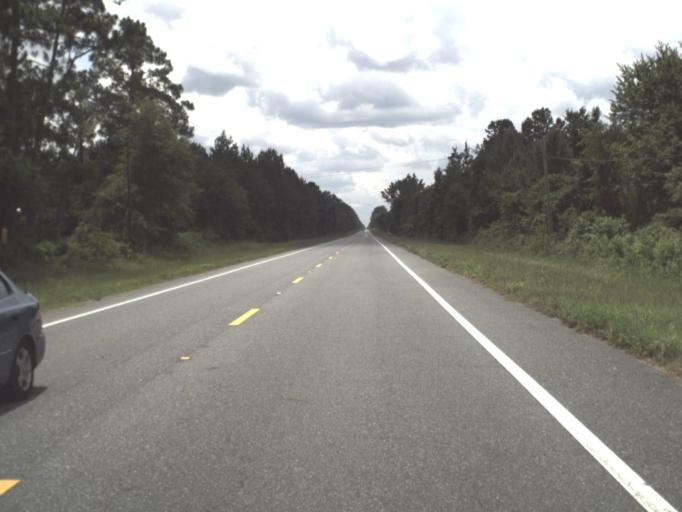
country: US
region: Florida
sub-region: Columbia County
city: Watertown
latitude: 30.1577
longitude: -82.5627
